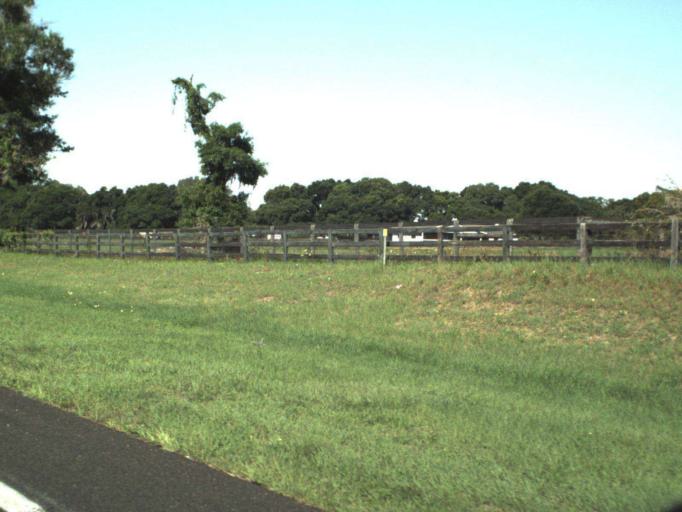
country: US
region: Florida
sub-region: Marion County
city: Citra
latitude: 29.3916
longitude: -82.1223
